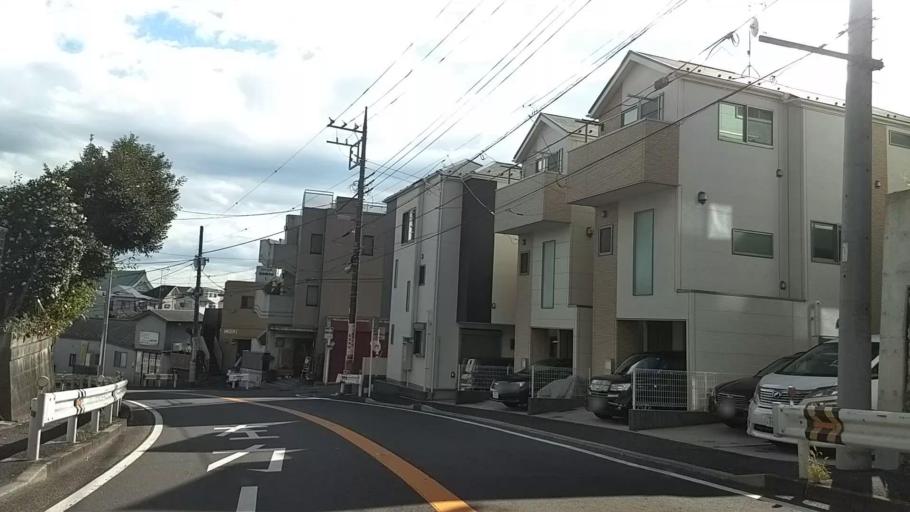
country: JP
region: Kanagawa
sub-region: Kawasaki-shi
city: Kawasaki
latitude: 35.5097
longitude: 139.6646
